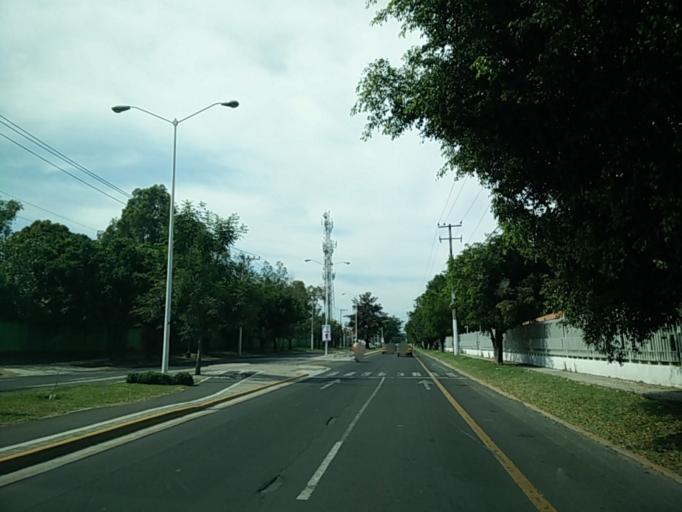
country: MX
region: Jalisco
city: Nuevo Mexico
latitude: 20.7307
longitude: -103.4476
